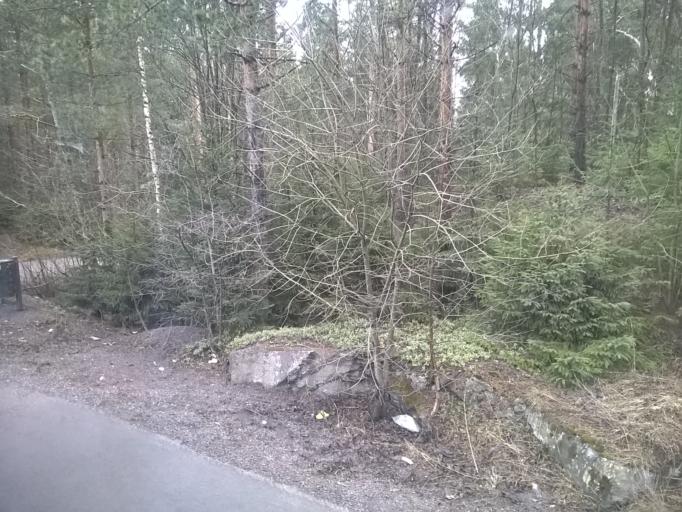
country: FI
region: Pirkanmaa
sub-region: Tampere
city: Tampere
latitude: 61.4629
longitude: 23.8442
